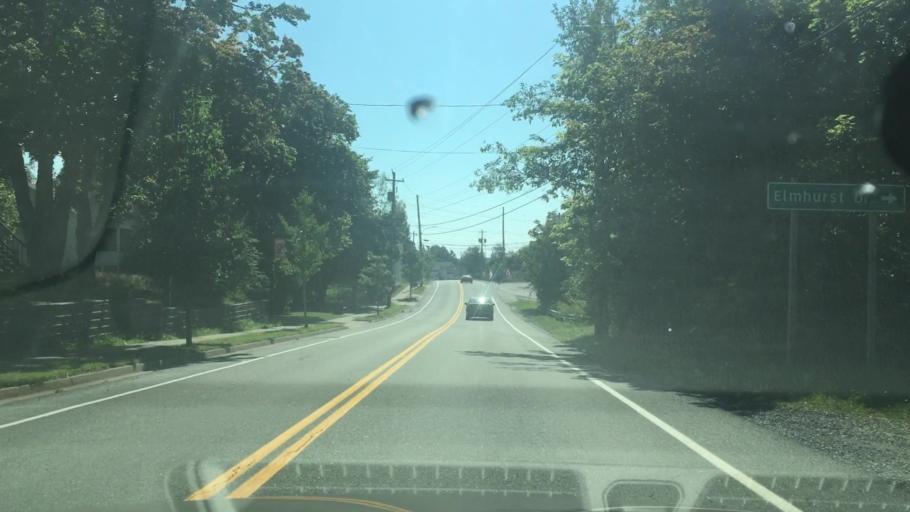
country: CA
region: Nova Scotia
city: New Glasgow
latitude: 44.9266
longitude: -62.5421
